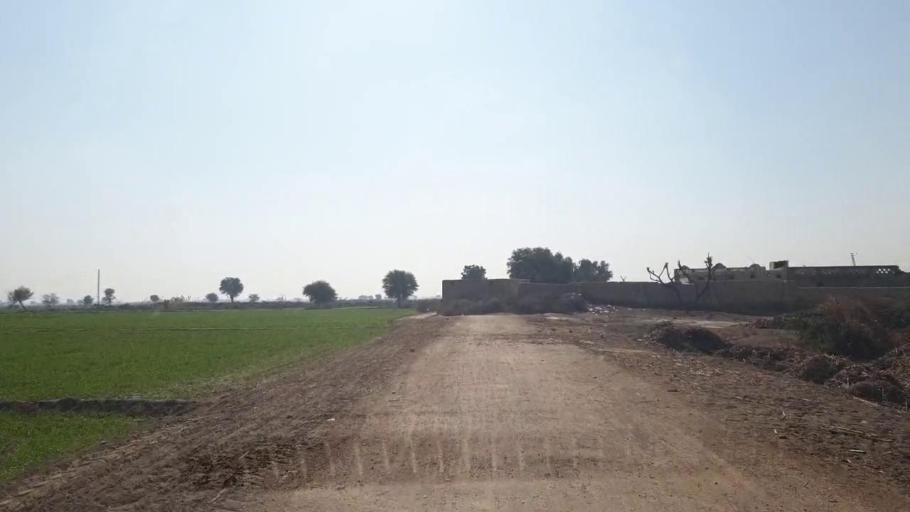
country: PK
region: Sindh
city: Shahpur Chakar
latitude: 26.1180
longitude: 68.6056
